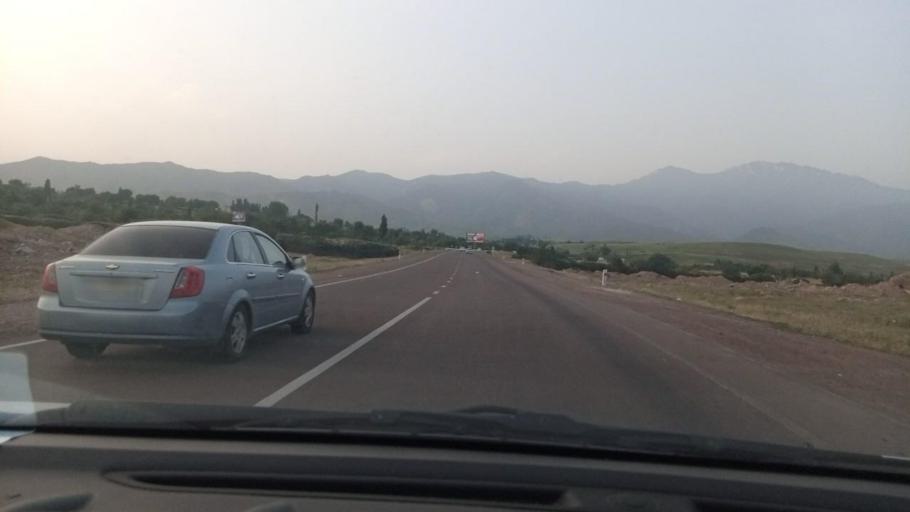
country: UZ
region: Toshkent
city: Angren
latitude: 41.0467
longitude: 70.1586
